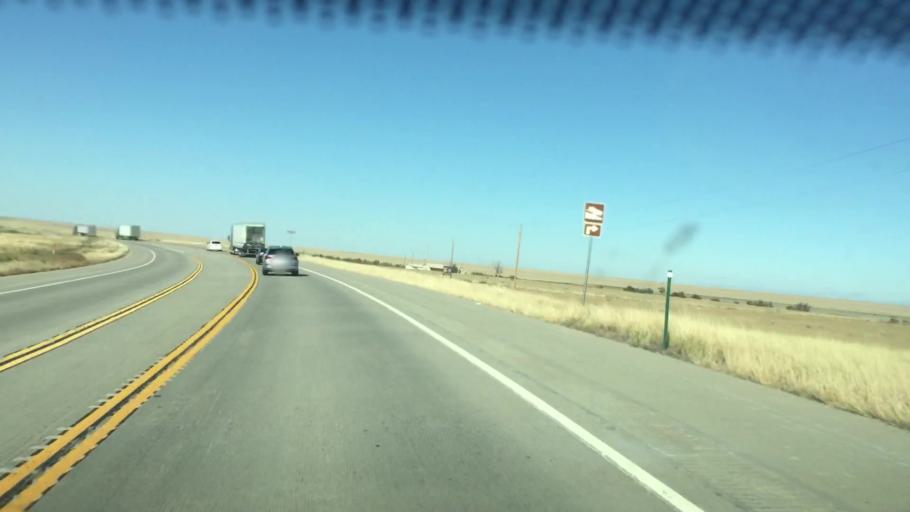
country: US
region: Colorado
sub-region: Kiowa County
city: Eads
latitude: 38.3467
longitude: -102.7149
